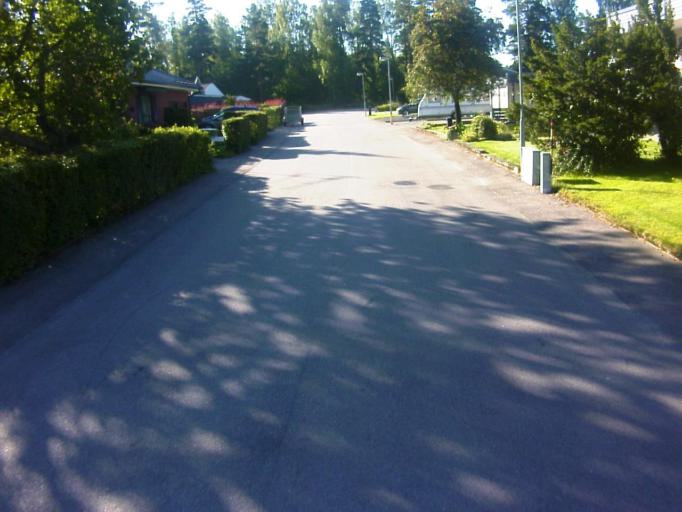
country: SE
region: Soedermanland
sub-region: Eskilstuna Kommun
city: Skogstorp
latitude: 59.3328
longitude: 16.4397
